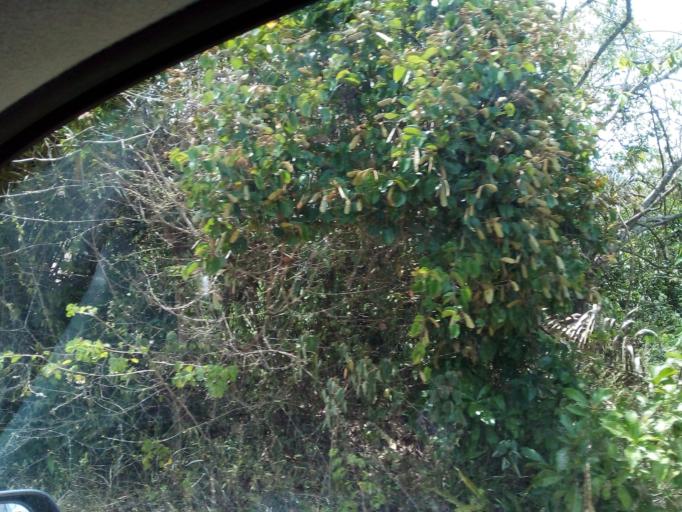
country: BR
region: Maranhao
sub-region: Itapecuru Mirim
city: Itapecuru Mirim
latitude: -3.1356
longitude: -44.3372
